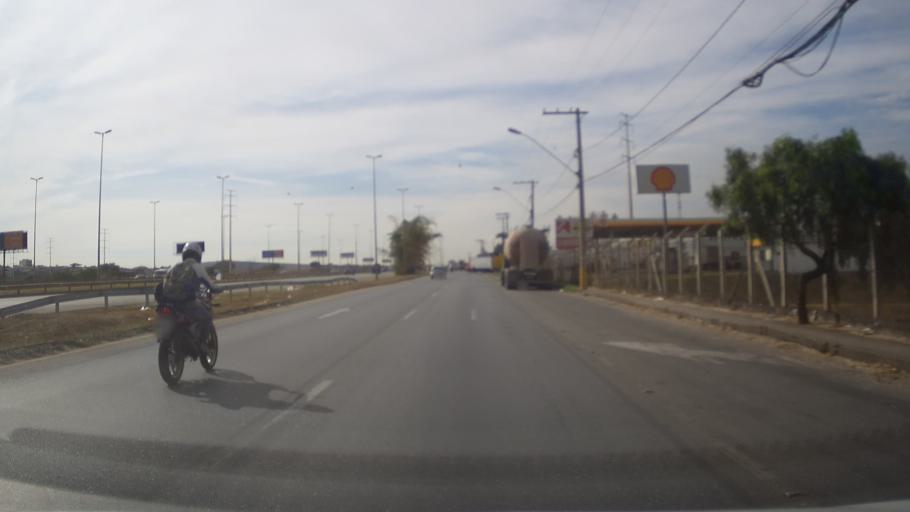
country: BR
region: Minas Gerais
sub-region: Contagem
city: Contagem
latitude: -19.9077
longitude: -44.0459
